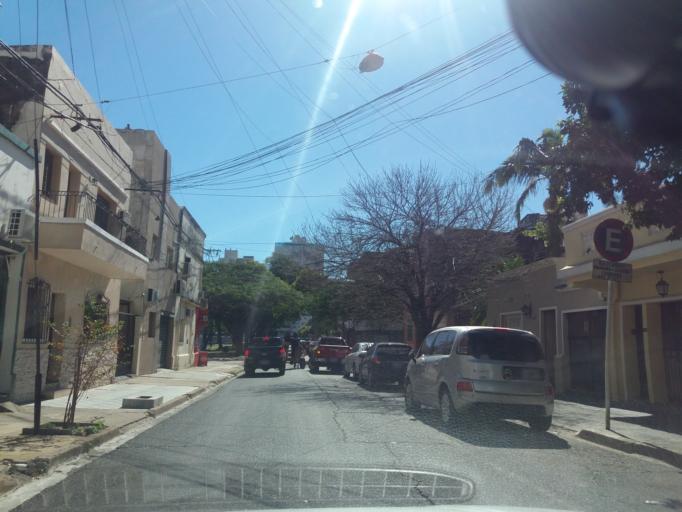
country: AR
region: Corrientes
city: Corrientes
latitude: -27.4664
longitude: -58.8429
